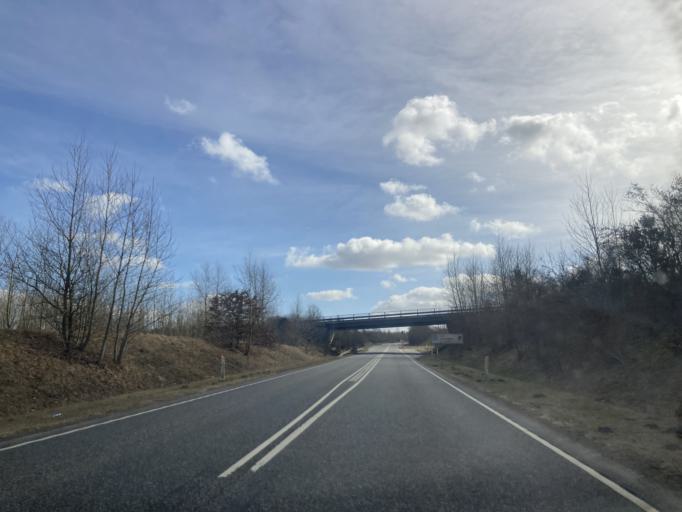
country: DK
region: Central Jutland
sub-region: Hedensted Kommune
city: Torring
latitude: 55.9702
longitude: 9.4012
